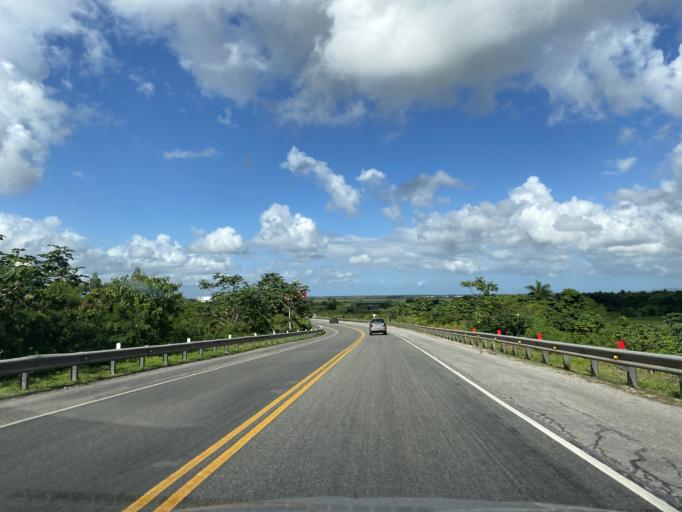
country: DO
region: Duarte
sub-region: Villa Riva
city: Agua Santa del Yuna
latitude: 19.1105
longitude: -69.8338
